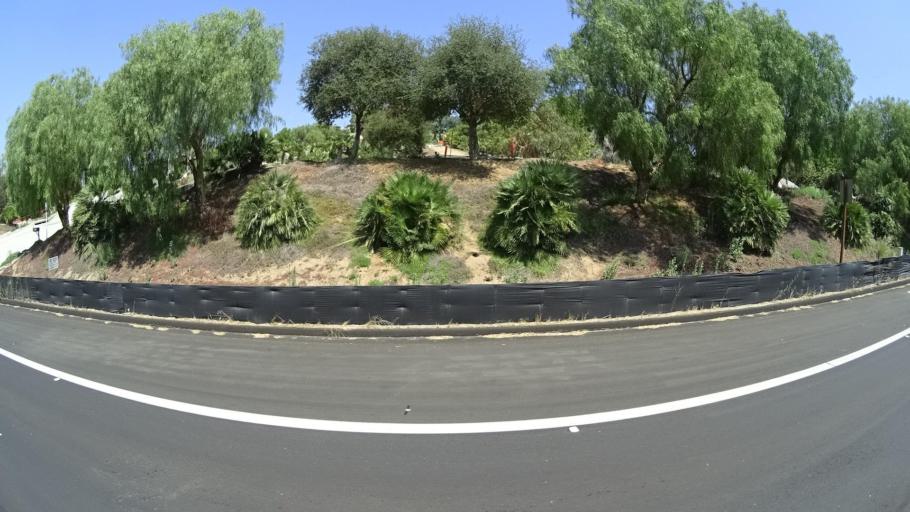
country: US
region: California
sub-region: San Diego County
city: Bonsall
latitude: 33.2824
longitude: -117.1965
